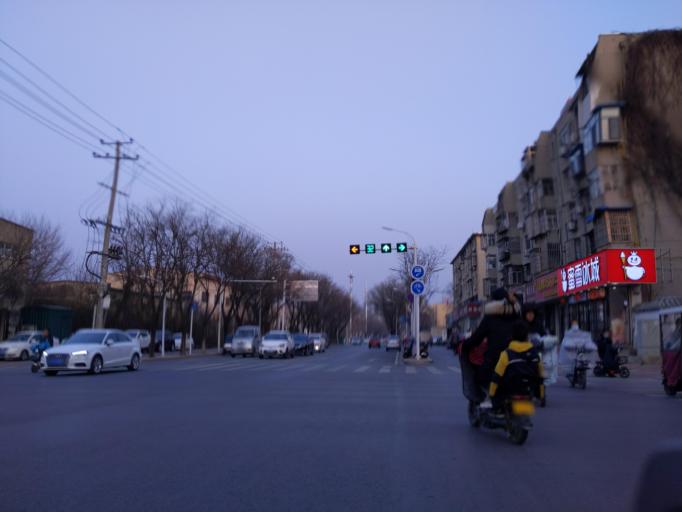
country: CN
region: Henan Sheng
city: Zhongyuanlu
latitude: 35.7698
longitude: 115.0909
